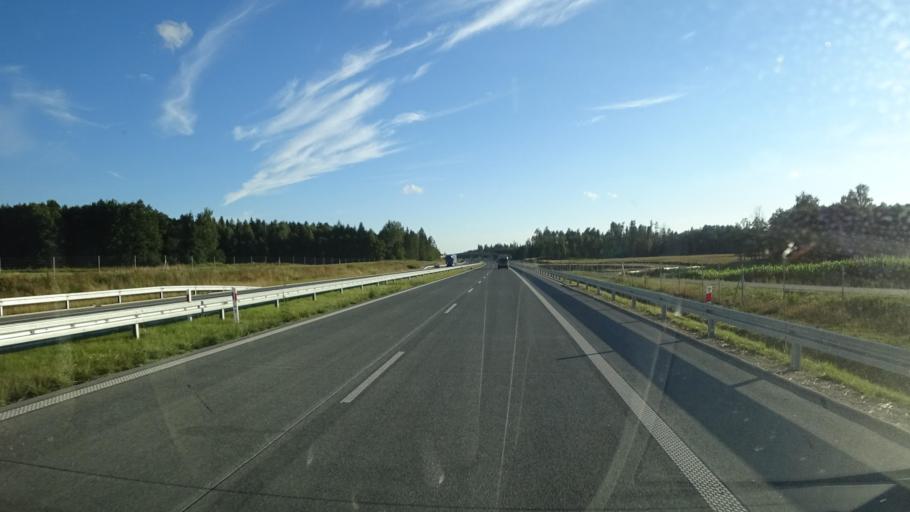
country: PL
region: Podlasie
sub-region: Powiat suwalski
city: Raczki
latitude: 53.9042
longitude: 22.7017
